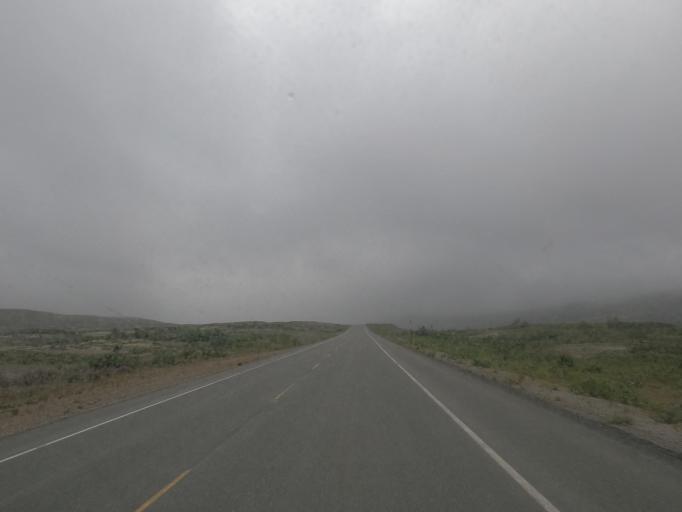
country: US
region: Alaska
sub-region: Haines Borough
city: Haines
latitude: 59.6817
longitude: -136.5753
